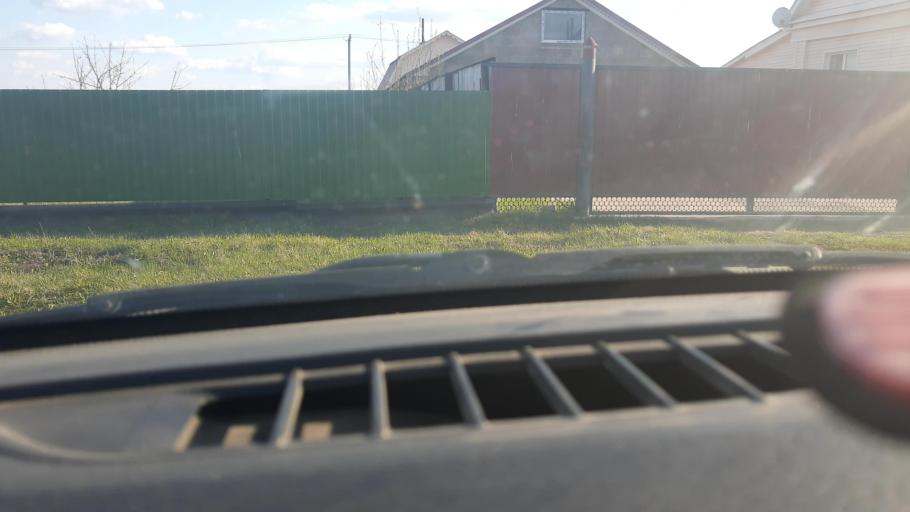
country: RU
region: Bashkortostan
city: Chishmy
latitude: 54.5970
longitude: 55.2694
